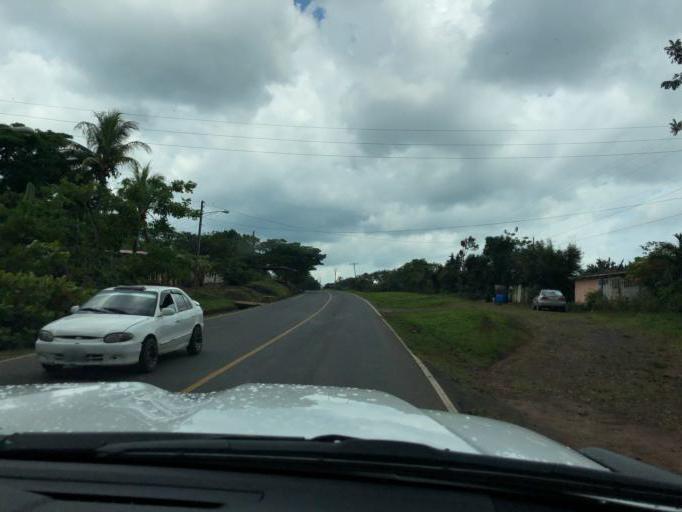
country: NI
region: Chontales
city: Villa Sandino
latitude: 11.9923
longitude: -84.8627
